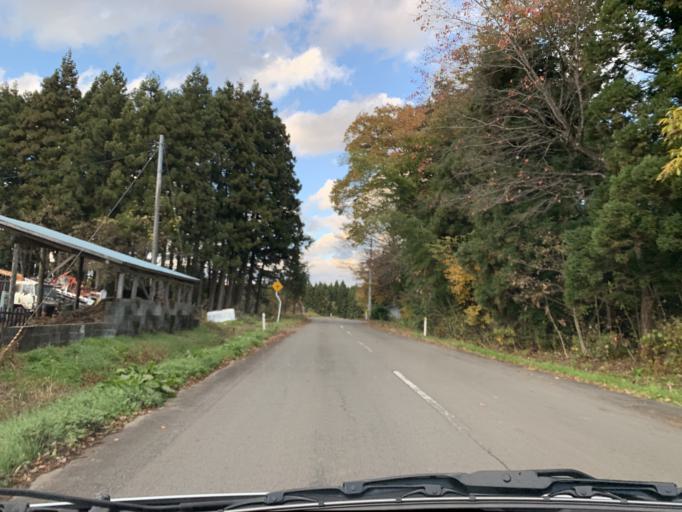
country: JP
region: Iwate
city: Mizusawa
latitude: 39.0996
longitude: 141.0148
